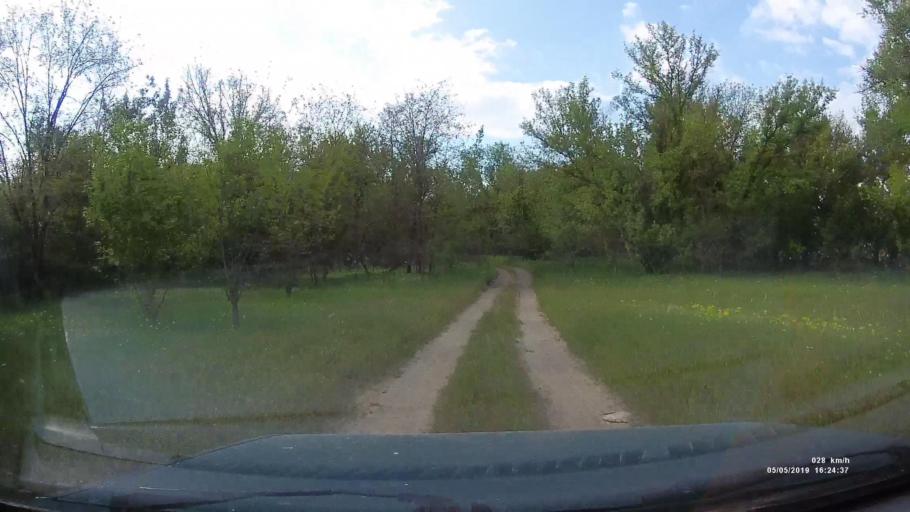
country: RU
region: Rostov
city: Konstantinovsk
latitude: 47.7599
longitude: 41.0254
